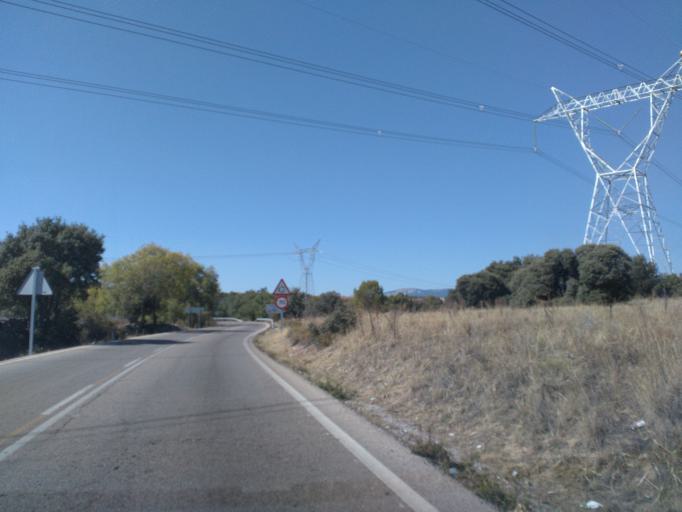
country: ES
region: Madrid
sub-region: Provincia de Madrid
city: Galapagar
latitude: 40.5782
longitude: -3.9868
